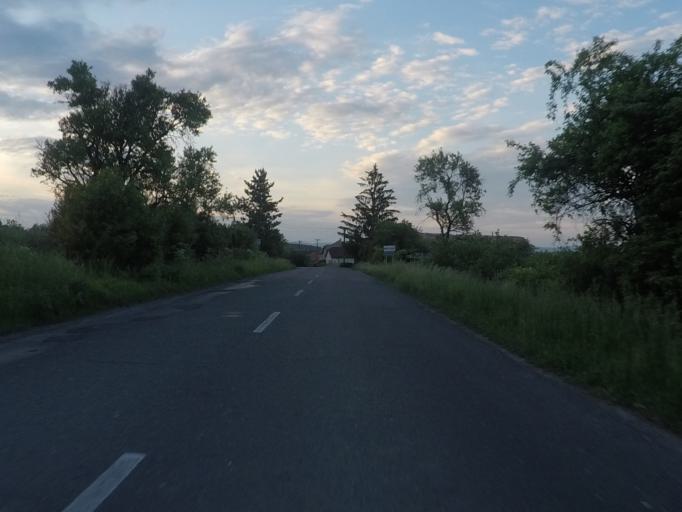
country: SK
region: Banskobystricky
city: Poltar
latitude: 48.3597
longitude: 19.8315
